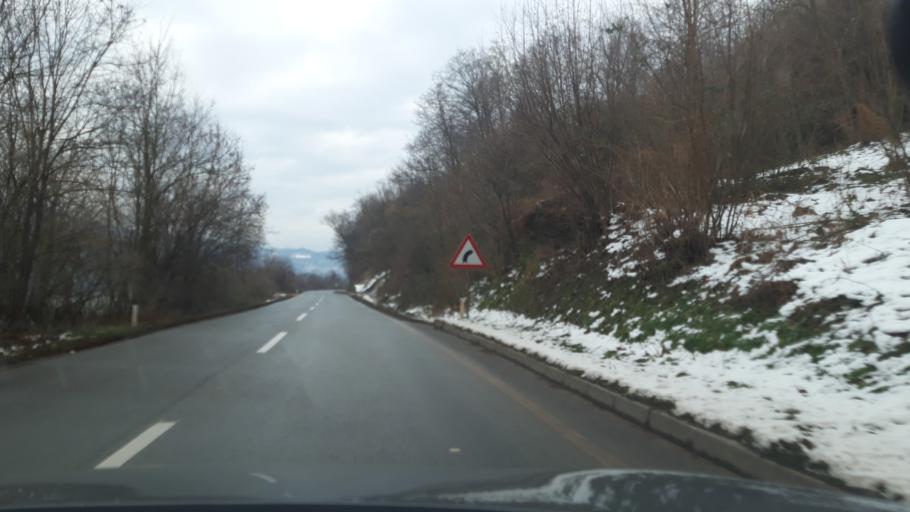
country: RS
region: Central Serbia
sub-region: Macvanski Okrug
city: Mali Zvornik
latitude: 44.3036
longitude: 19.1424
